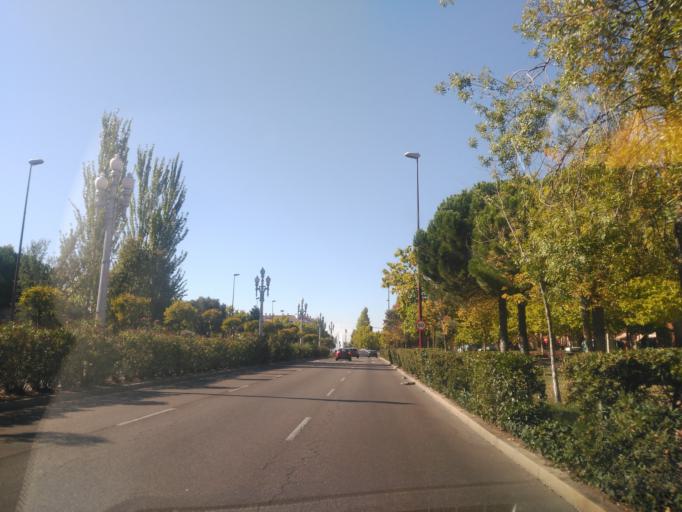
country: ES
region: Castille and Leon
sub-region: Provincia de Valladolid
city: Valladolid
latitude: 41.6273
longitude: -4.7443
